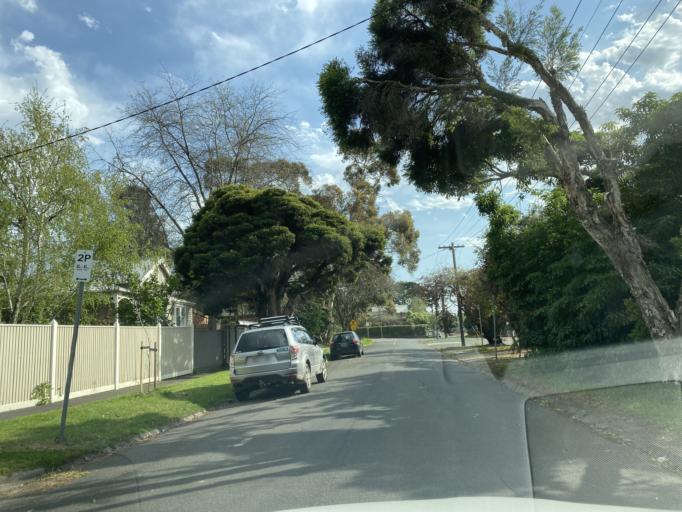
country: AU
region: Victoria
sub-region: Boroondara
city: Camberwell
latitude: -37.8305
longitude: 145.0694
